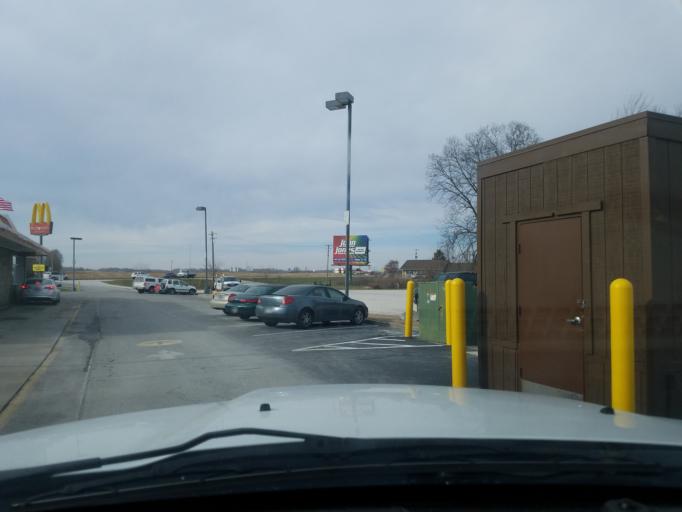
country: US
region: Indiana
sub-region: Lawrence County
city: Mitchell
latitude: 38.7248
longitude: -86.4783
